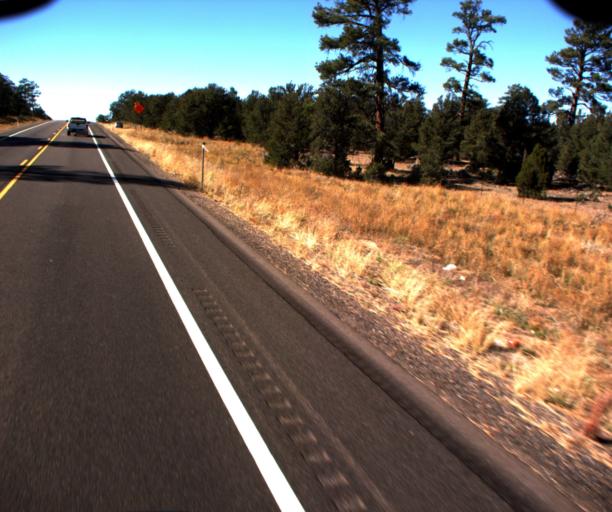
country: US
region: Arizona
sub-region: Apache County
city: Ganado
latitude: 35.7080
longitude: -109.3173
